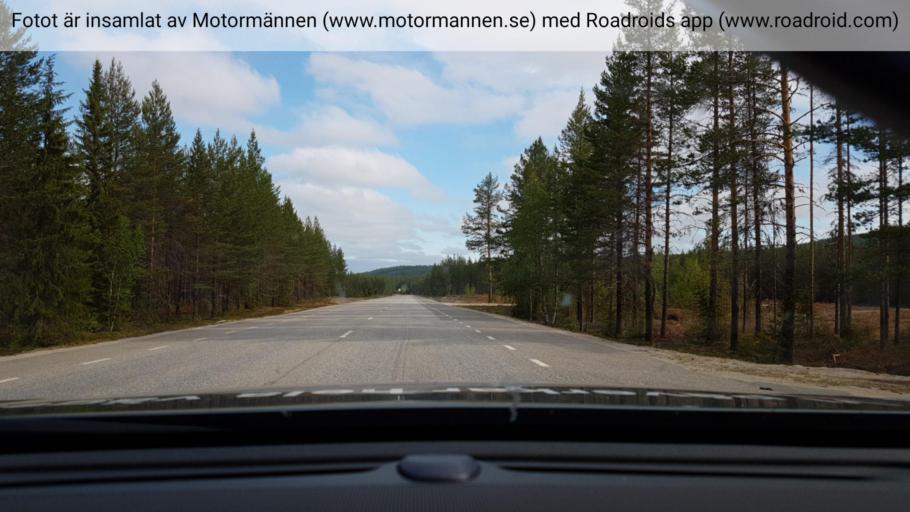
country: SE
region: Vaesterbotten
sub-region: Norsjo Kommun
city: Norsjoe
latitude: 64.5964
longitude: 19.2989
